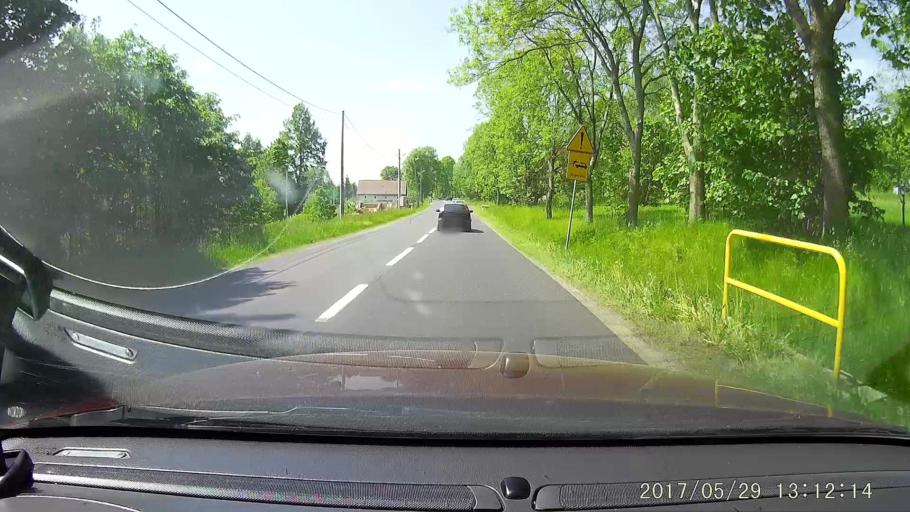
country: PL
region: Lower Silesian Voivodeship
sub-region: Powiat lwowecki
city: Lubomierz
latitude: 50.9674
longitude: 15.5093
